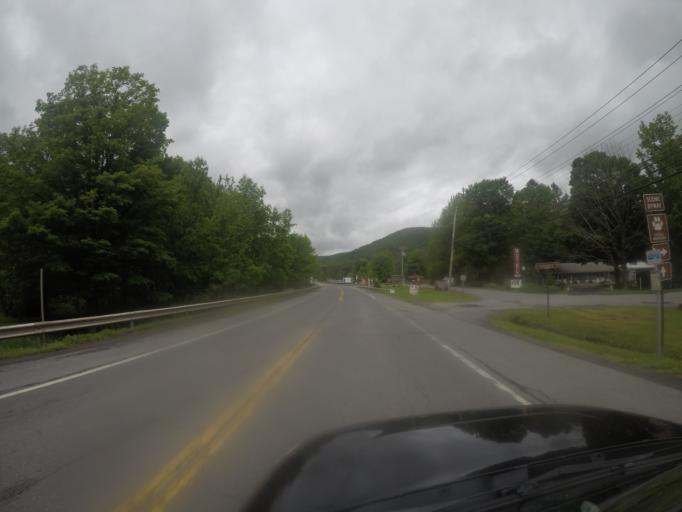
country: US
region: New York
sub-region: Ulster County
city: Shokan
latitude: 42.1193
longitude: -74.3919
